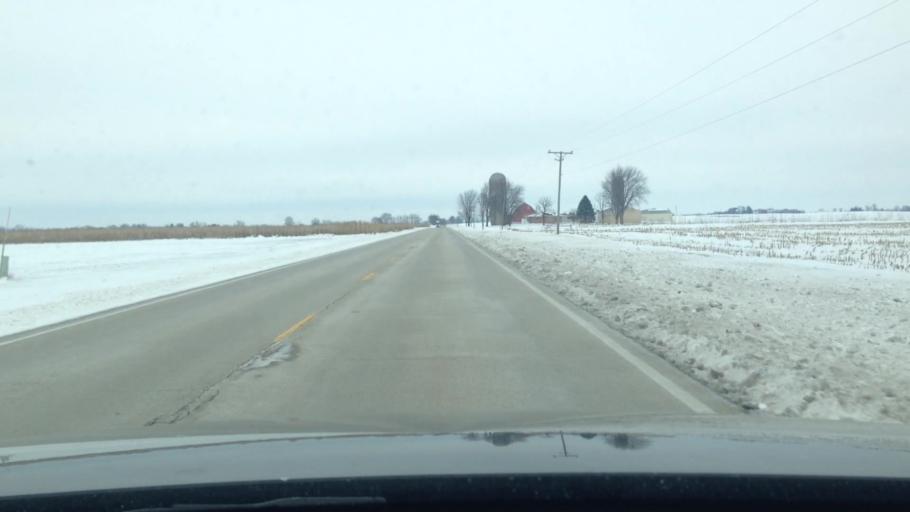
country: US
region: Illinois
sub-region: McHenry County
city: Hebron
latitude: 42.4237
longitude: -88.4381
